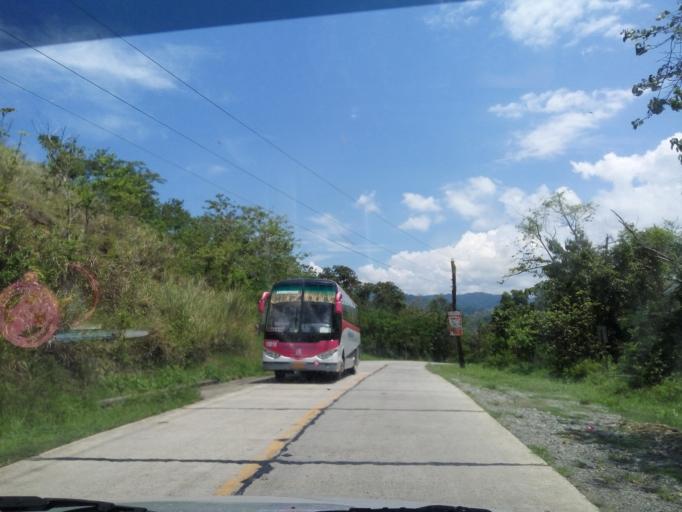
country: PH
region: Central Luzon
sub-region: Province of Nueva Ecija
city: General Luna
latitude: 15.7971
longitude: 121.2983
